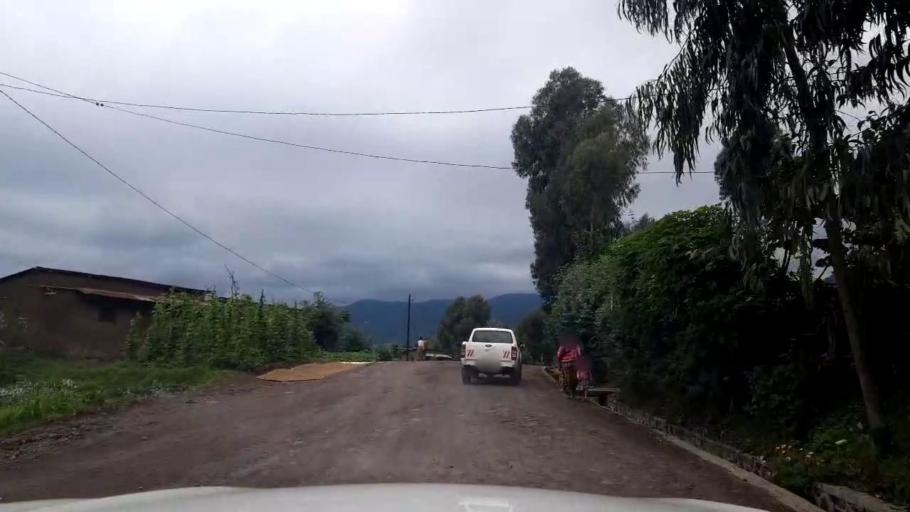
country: RW
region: Northern Province
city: Musanze
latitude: -1.4458
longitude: 29.5310
